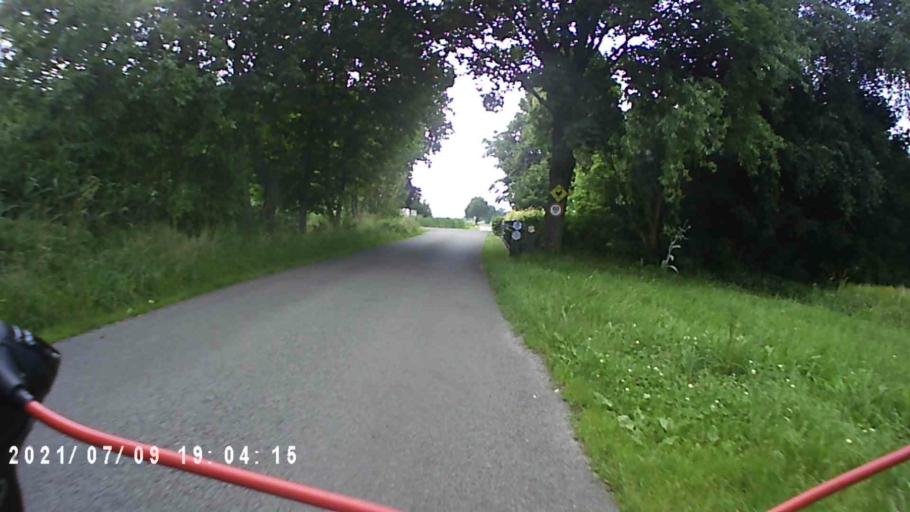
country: NL
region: Groningen
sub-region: Gemeente Veendam
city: Veendam
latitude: 53.0508
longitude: 6.8874
